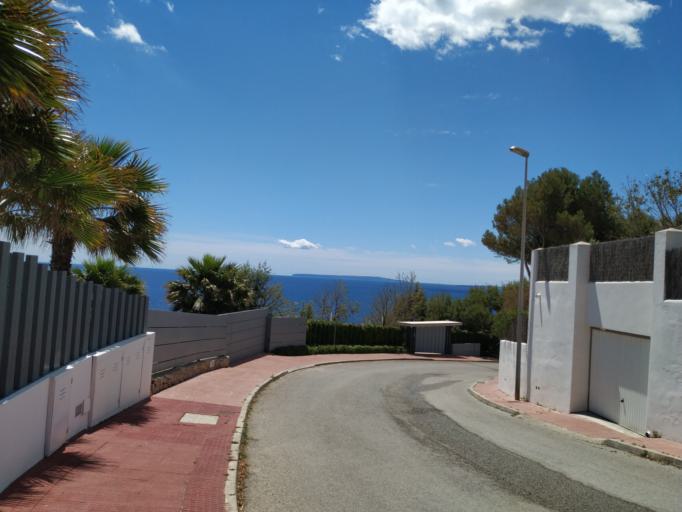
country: ES
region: Balearic Islands
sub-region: Illes Balears
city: Ibiza
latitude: 38.9171
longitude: 1.4745
